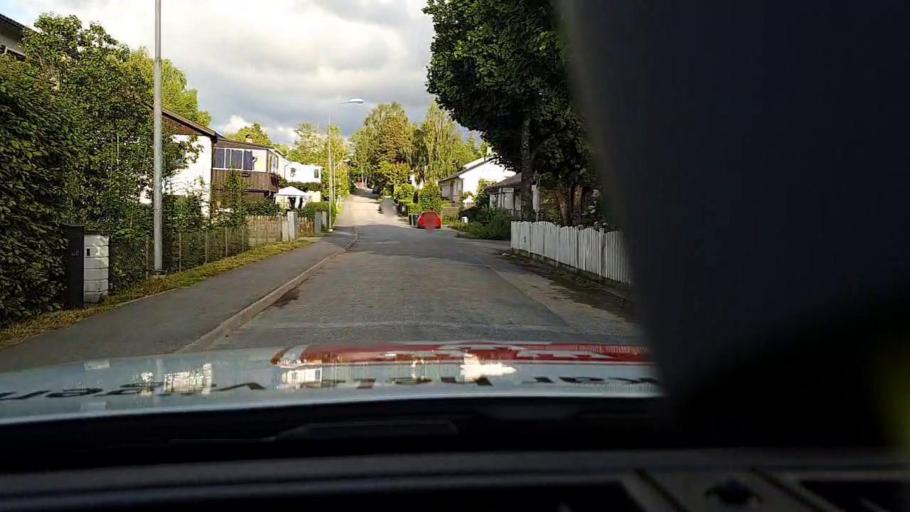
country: SE
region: Stockholm
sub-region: Huddinge Kommun
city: Huddinge
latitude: 59.2488
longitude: 17.9632
